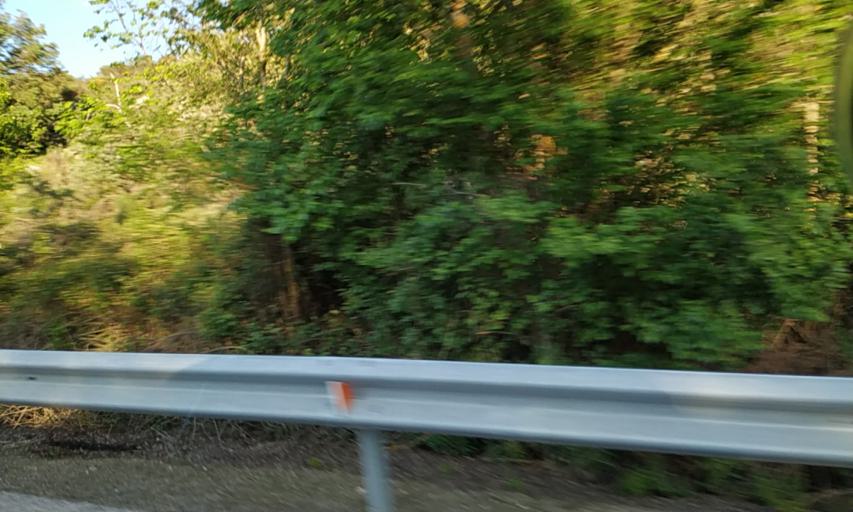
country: ES
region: Extremadura
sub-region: Provincia de Caceres
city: Valencia de Alcantara
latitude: 39.3819
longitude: -7.2490
